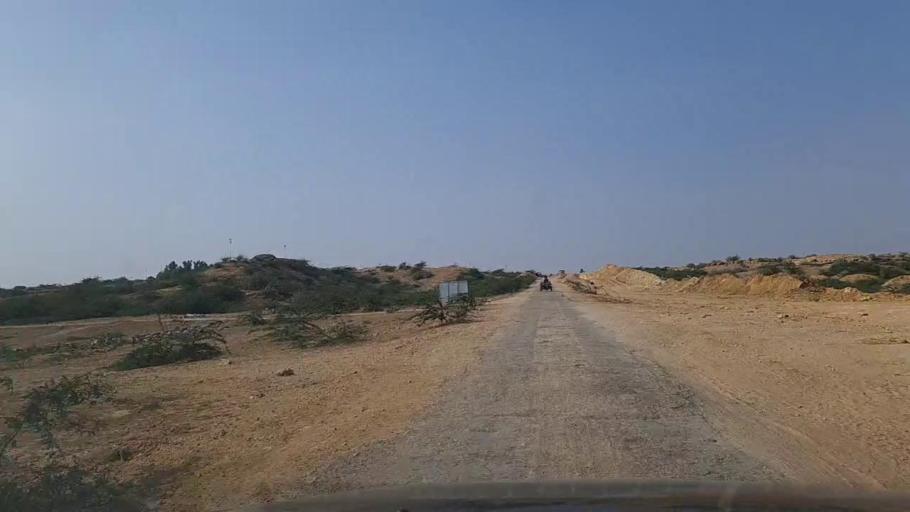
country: PK
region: Sindh
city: Gharo
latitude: 24.7687
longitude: 67.5753
